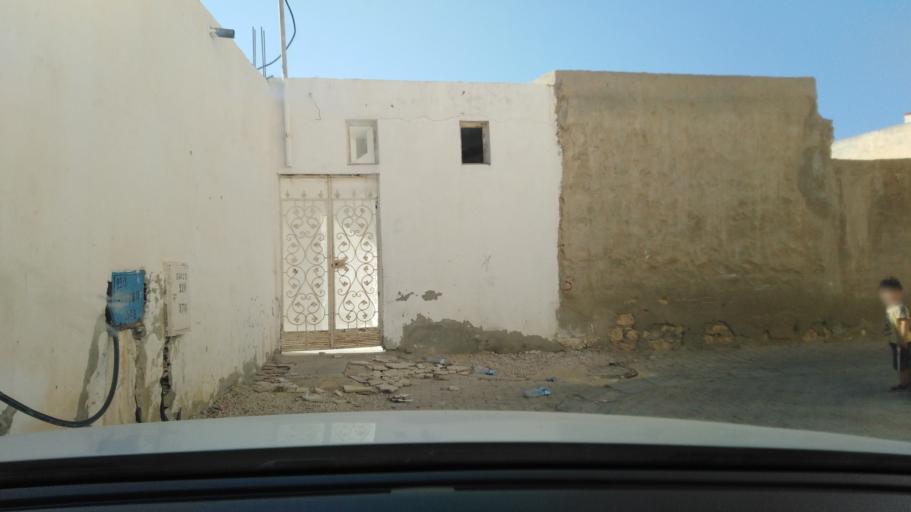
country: TN
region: Qabis
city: Gabes
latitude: 33.9379
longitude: 10.0698
